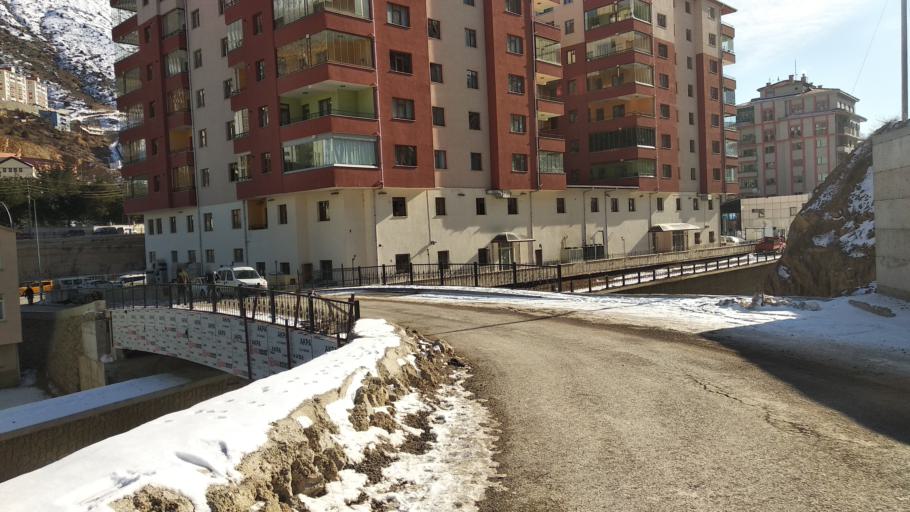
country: TR
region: Gumushane
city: Gumushkhane
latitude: 40.4503
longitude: 39.4943
